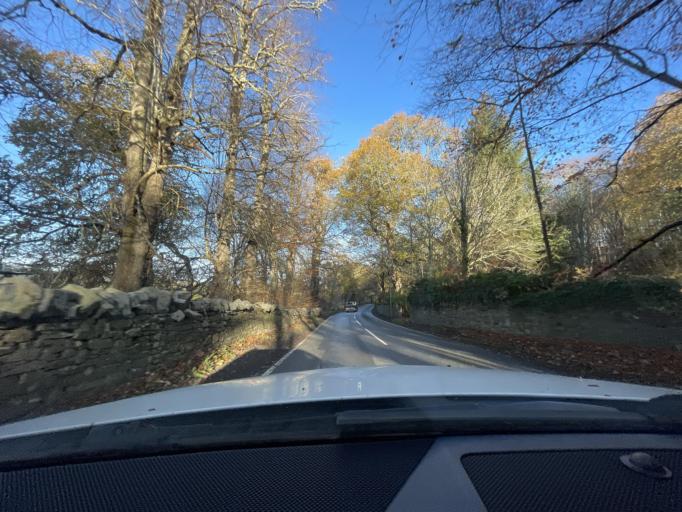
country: GB
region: Scotland
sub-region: Highland
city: Inverness
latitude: 57.4448
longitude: -4.2586
